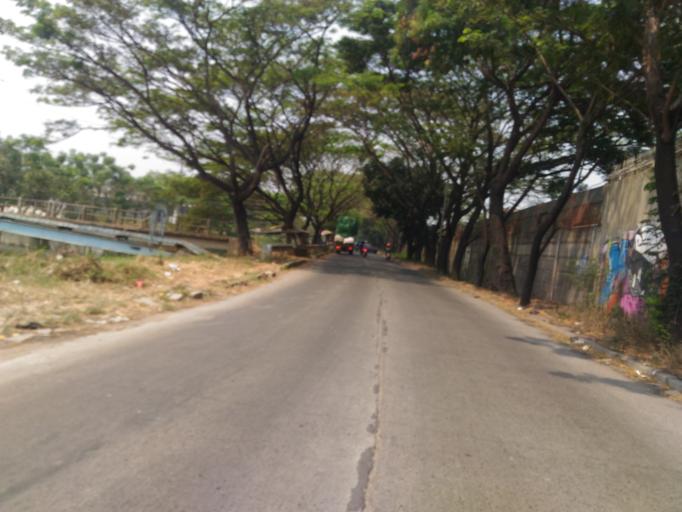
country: ID
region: Banten
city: Tangerang
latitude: -6.1584
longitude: 106.6101
